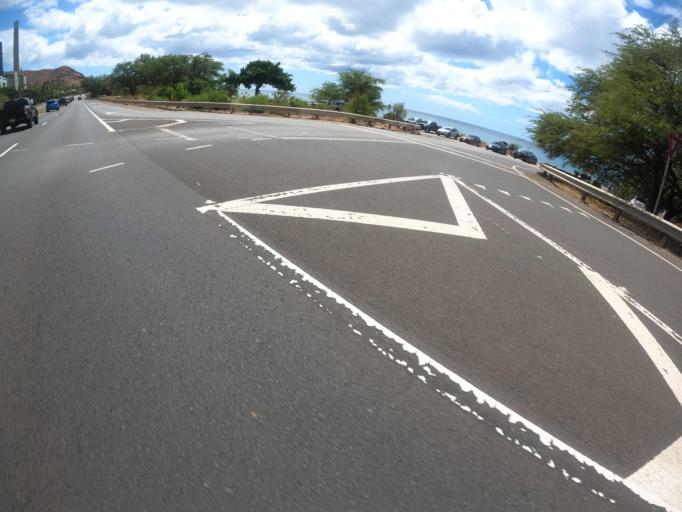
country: US
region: Hawaii
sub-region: Honolulu County
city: Nanakuli
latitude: 21.3600
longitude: -158.1315
